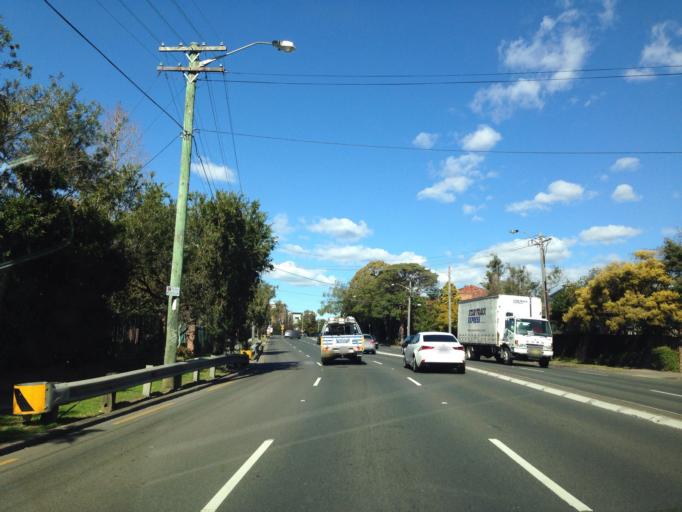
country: AU
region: New South Wales
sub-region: Ku-ring-gai
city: Killara
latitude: -33.7592
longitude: 151.1541
